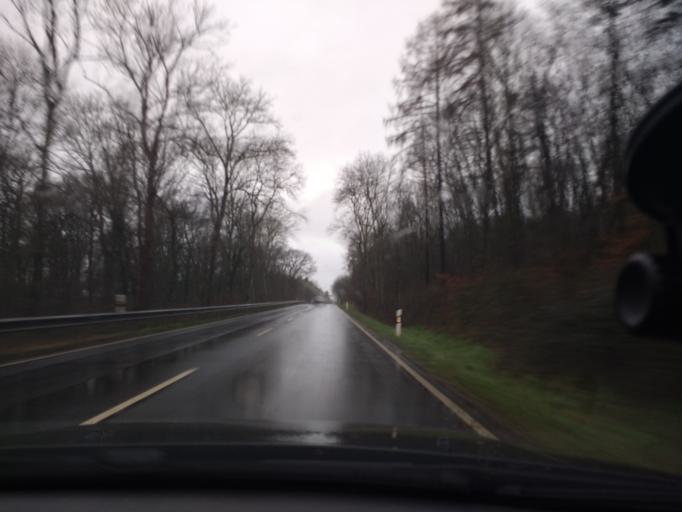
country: DE
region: Rheinland-Pfalz
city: Pellingen
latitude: 49.7010
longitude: 6.6354
